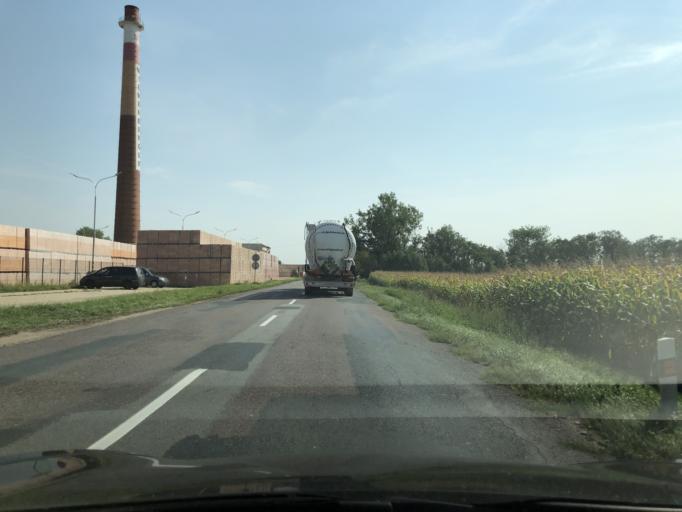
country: CZ
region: South Moravian
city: Novosedly
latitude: 48.8355
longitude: 16.5117
